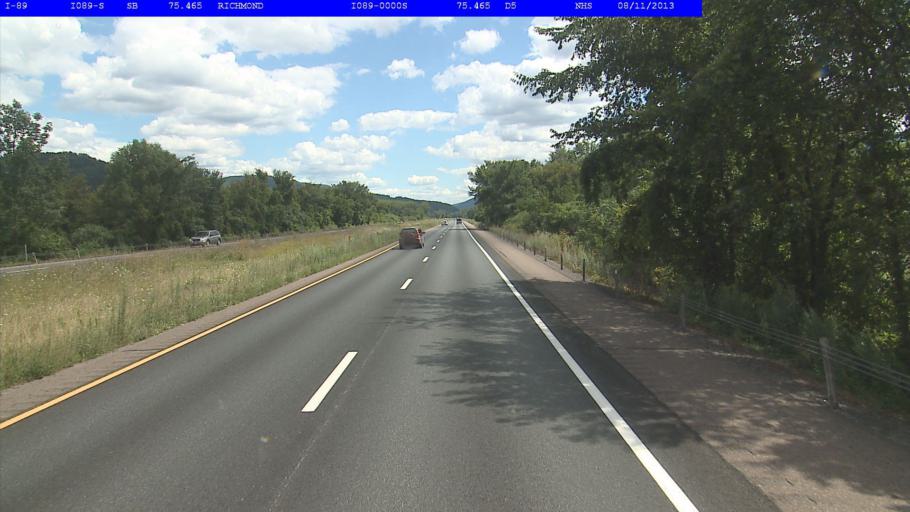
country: US
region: Vermont
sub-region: Chittenden County
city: Williston
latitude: 44.3961
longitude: -72.9706
